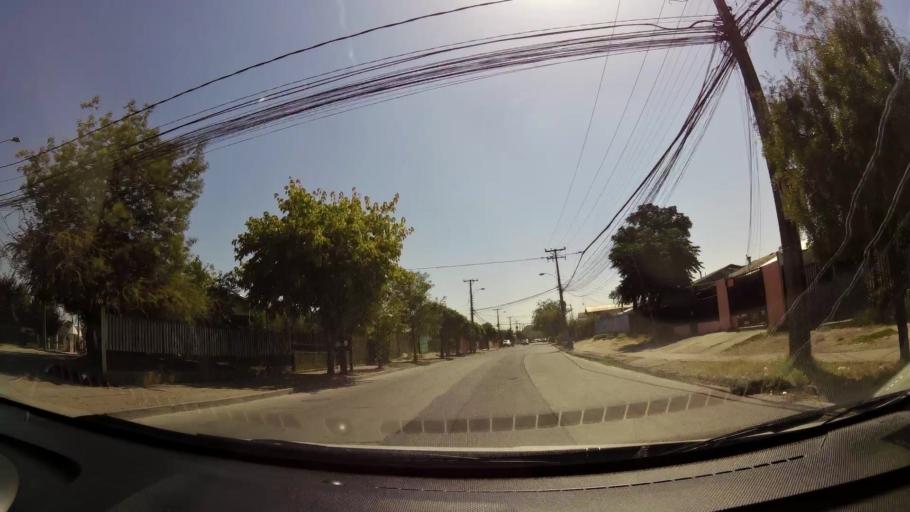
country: CL
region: Maule
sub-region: Provincia de Talca
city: Talca
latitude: -35.4181
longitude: -71.6431
